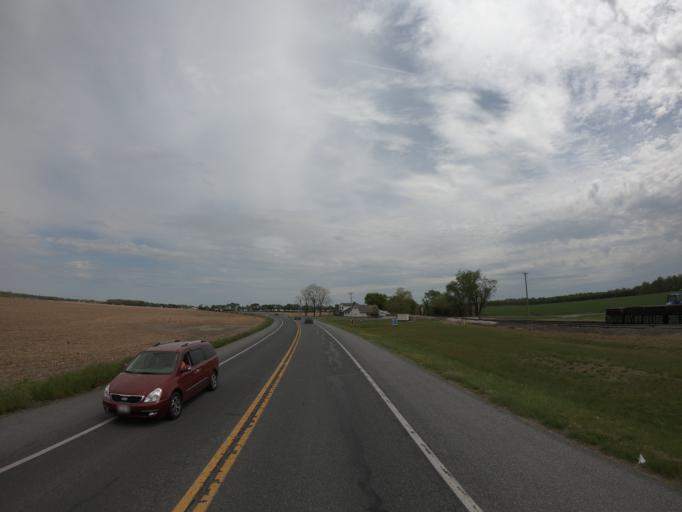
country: US
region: Delaware
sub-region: Sussex County
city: Milton
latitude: 38.7851
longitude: -75.3586
